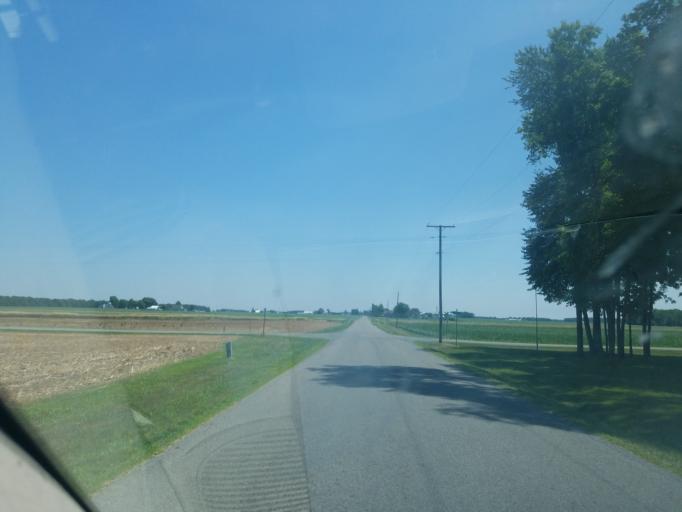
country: US
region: Ohio
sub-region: Allen County
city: Spencerville
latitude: 40.7576
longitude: -84.3883
